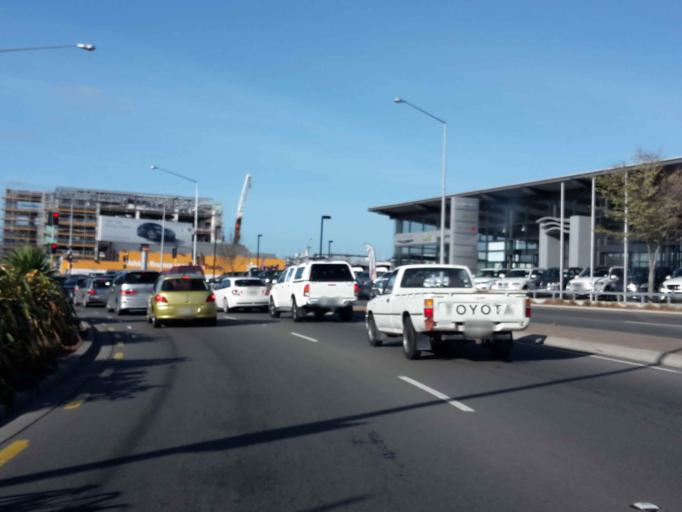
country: NZ
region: Canterbury
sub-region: Christchurch City
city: Christchurch
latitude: -43.5402
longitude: 172.6111
